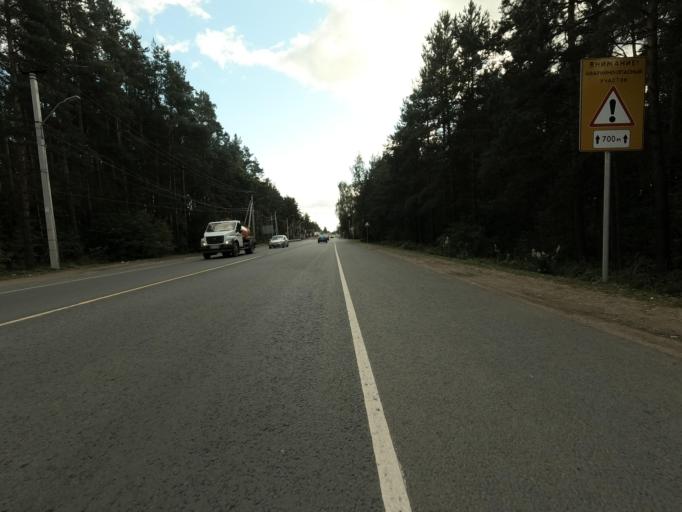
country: RU
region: Leningrad
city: Vsevolozhsk
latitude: 59.9937
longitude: 30.6590
